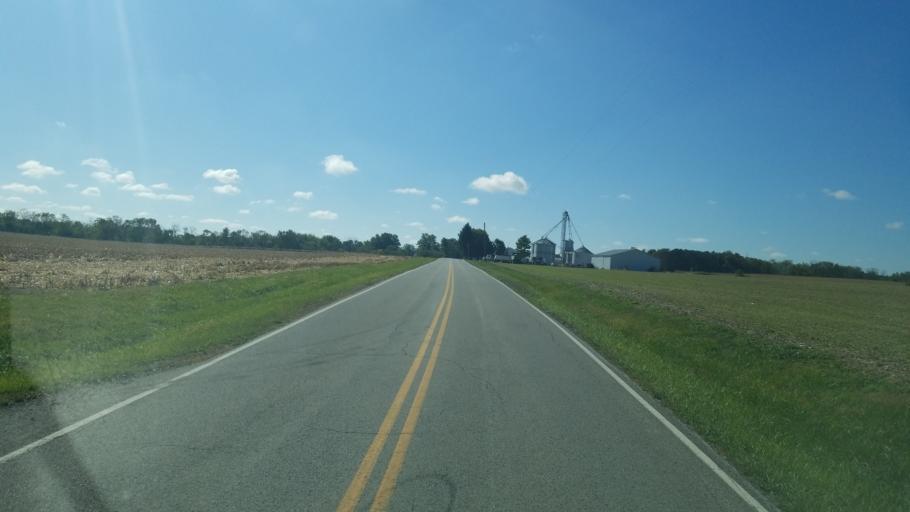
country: US
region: Ohio
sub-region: Highland County
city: Leesburg
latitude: 39.2959
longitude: -83.5797
